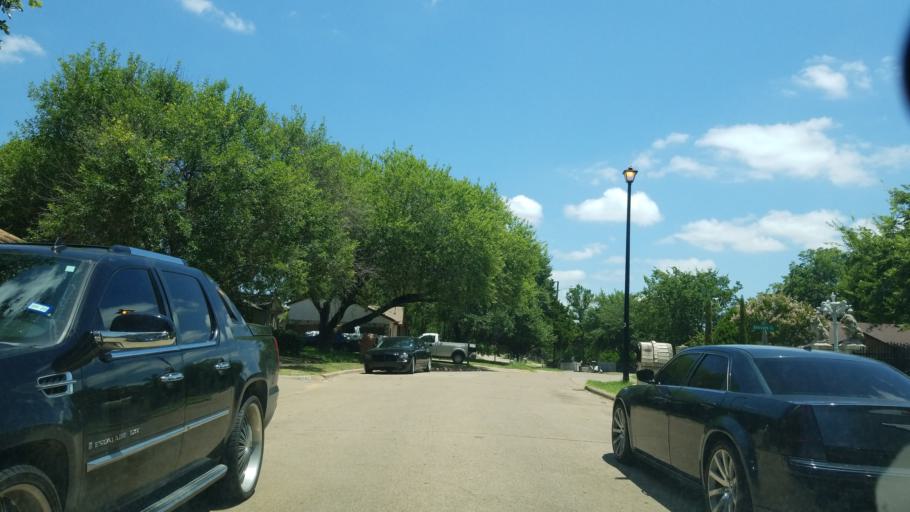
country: US
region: Texas
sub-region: Dallas County
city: Balch Springs
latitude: 32.7432
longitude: -96.7047
